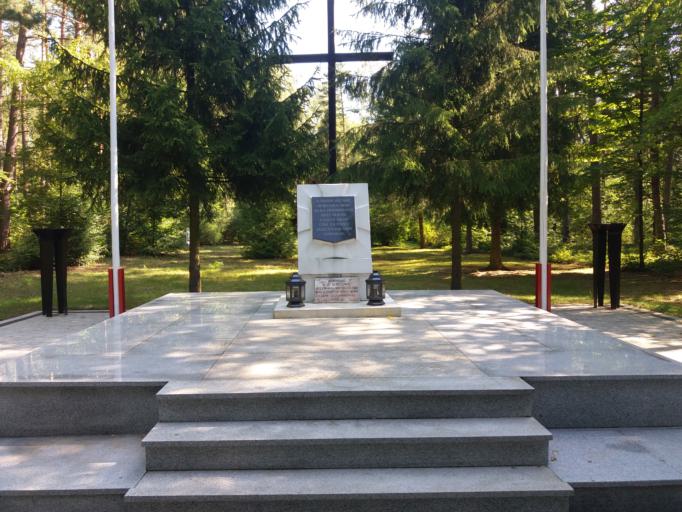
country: PL
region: Warmian-Masurian Voivodeship
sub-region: Powiat dzialdowski
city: Ilowo -Osada
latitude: 53.2043
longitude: 20.3473
